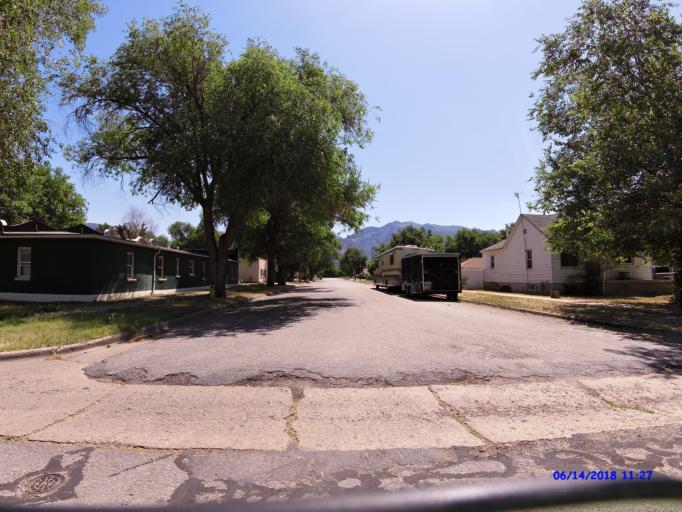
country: US
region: Utah
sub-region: Weber County
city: Ogden
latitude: 41.2220
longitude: -111.9927
